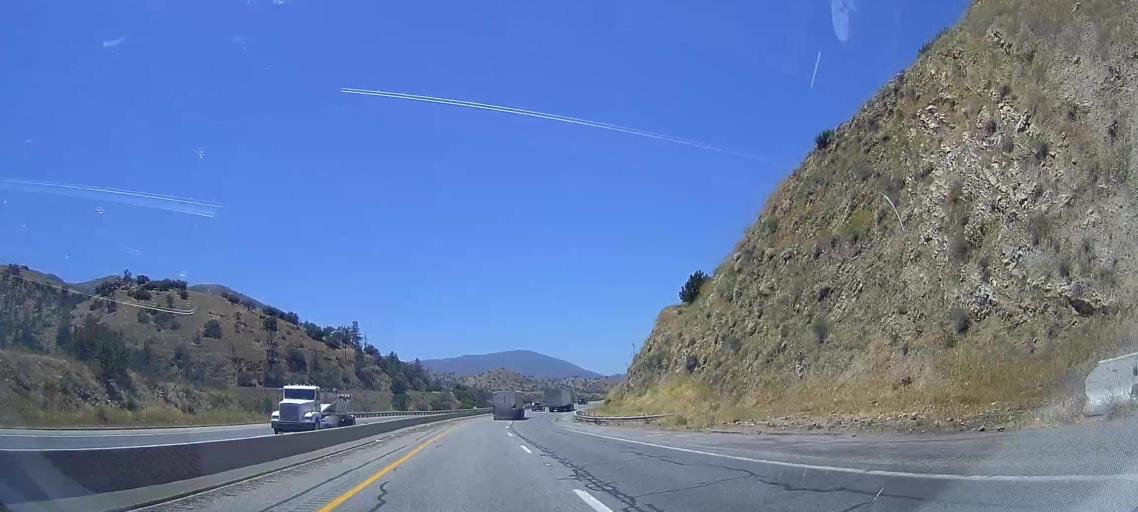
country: US
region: California
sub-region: Kern County
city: Golden Hills
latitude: 35.1820
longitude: -118.4945
